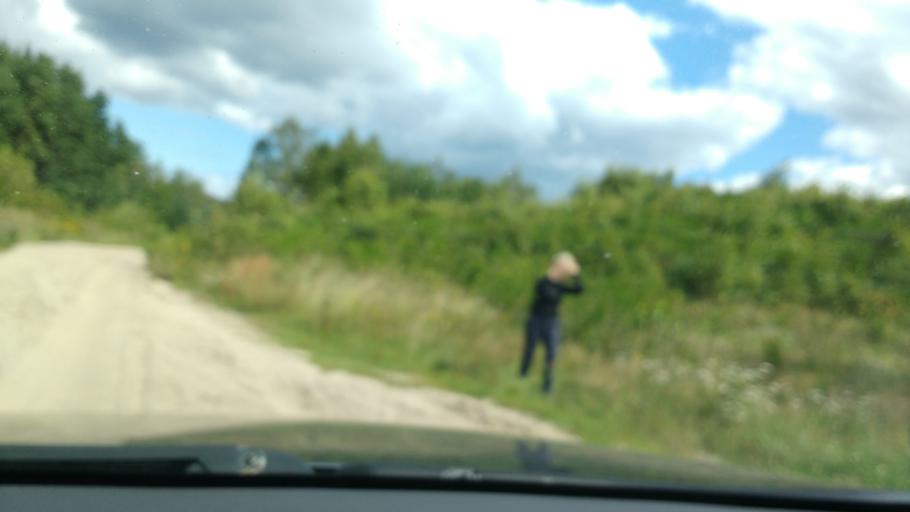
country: PL
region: Pomeranian Voivodeship
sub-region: Powiat kartuski
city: Chwaszczyno
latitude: 54.4745
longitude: 18.4362
